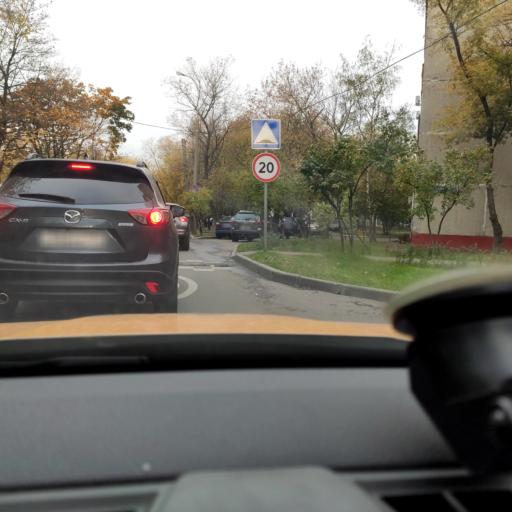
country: RU
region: Moscow
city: Tekstil'shchiki
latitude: 55.7053
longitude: 37.7387
